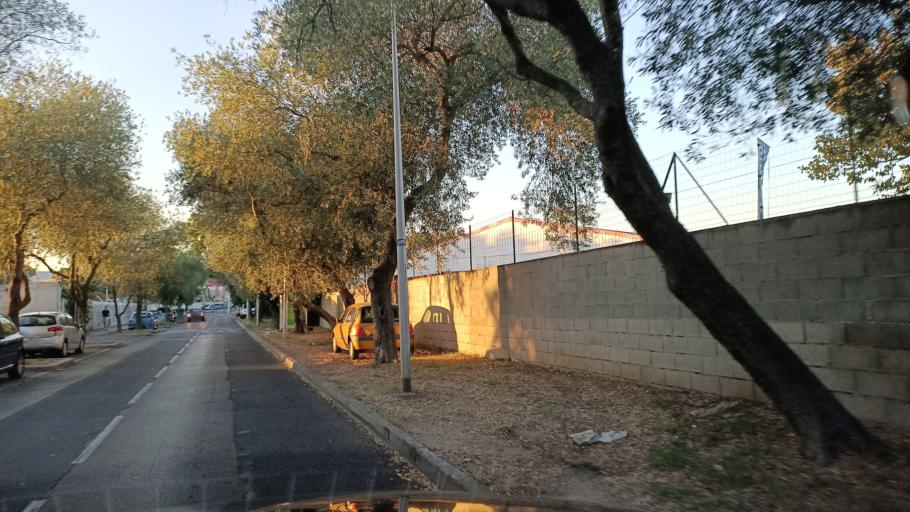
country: FR
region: Languedoc-Roussillon
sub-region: Departement de l'Herault
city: Saint-Jean-de-Vedas
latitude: 43.5867
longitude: 3.8552
